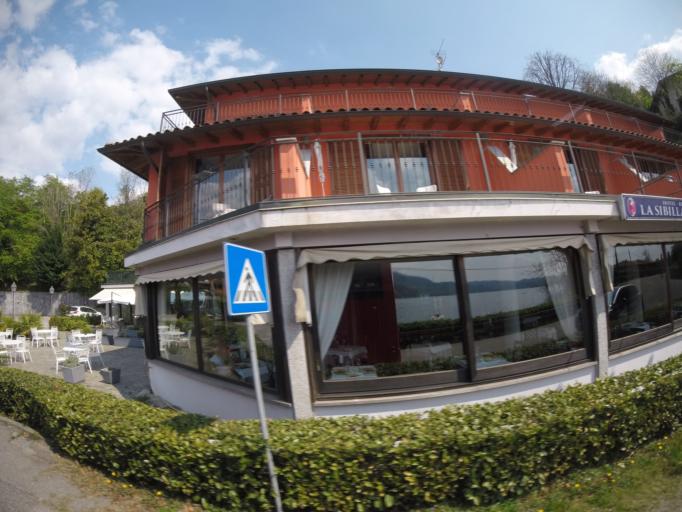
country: IT
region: Piedmont
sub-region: Provincia di Novara
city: Pettenasco
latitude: 45.8292
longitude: 8.3969
